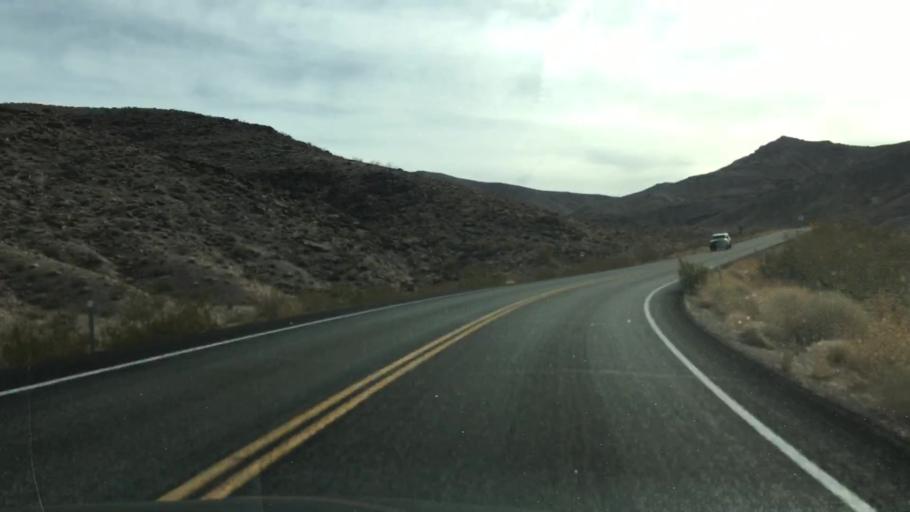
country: US
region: Nevada
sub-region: Nye County
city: Beatty
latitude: 36.7479
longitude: -116.9504
